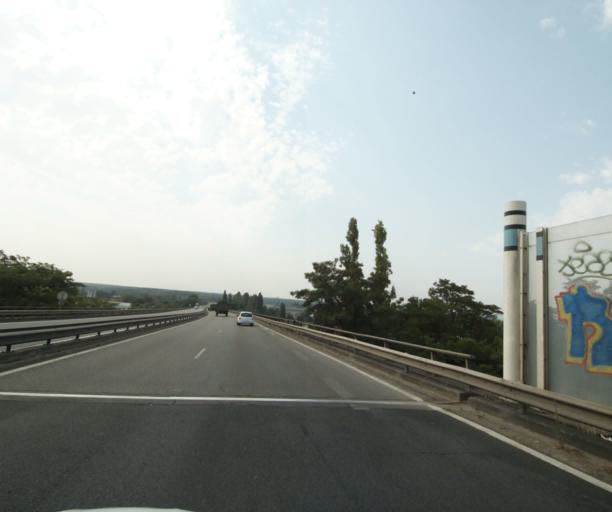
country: FR
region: Ile-de-France
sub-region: Departement des Yvelines
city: Conflans-Sainte-Honorine
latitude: 48.9907
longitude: 2.0815
